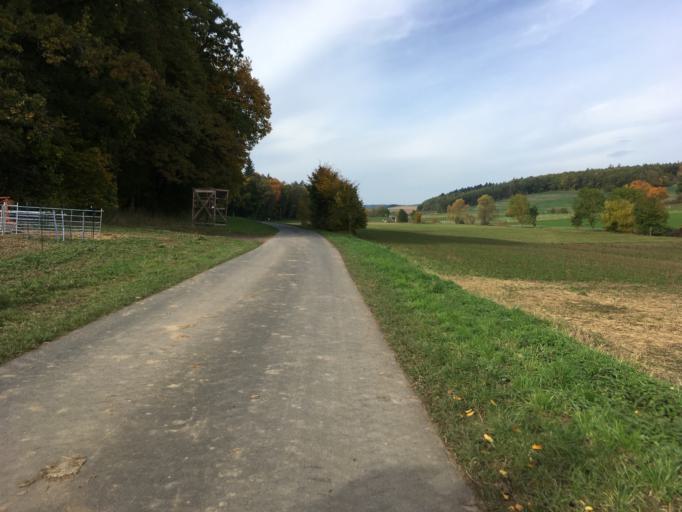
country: DE
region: Baden-Wuerttemberg
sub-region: Karlsruhe Region
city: Rosenberg
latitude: 49.4914
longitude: 9.4487
